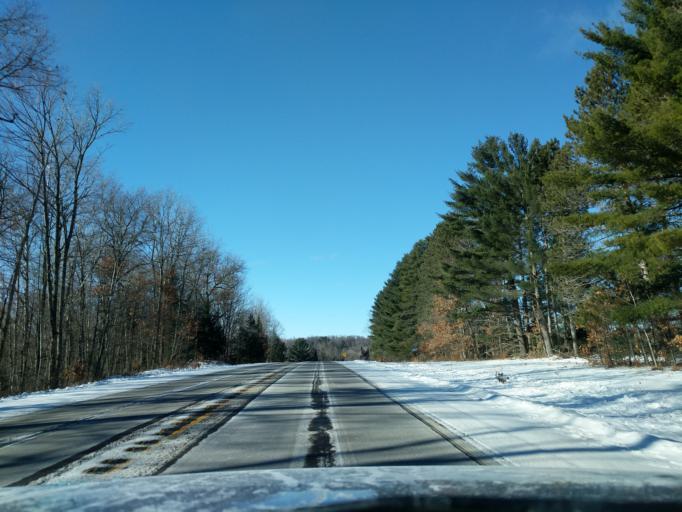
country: US
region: Wisconsin
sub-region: Menominee County
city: Keshena
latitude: 45.1181
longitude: -88.6590
